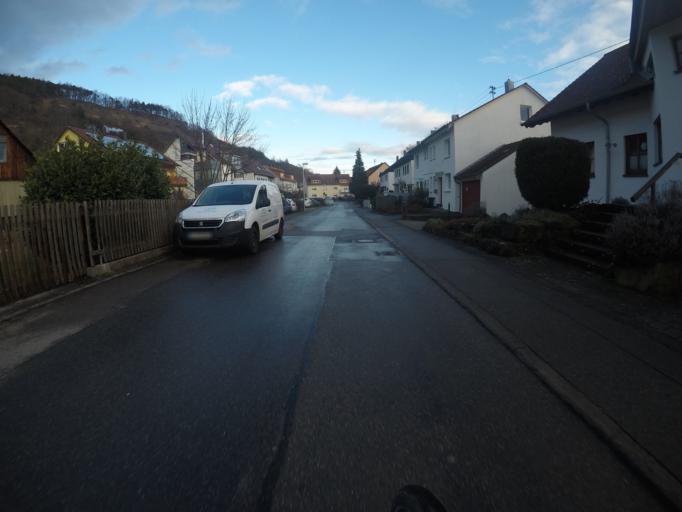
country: DE
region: Baden-Wuerttemberg
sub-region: Tuebingen Region
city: Tuebingen
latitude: 48.5020
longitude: 9.0014
